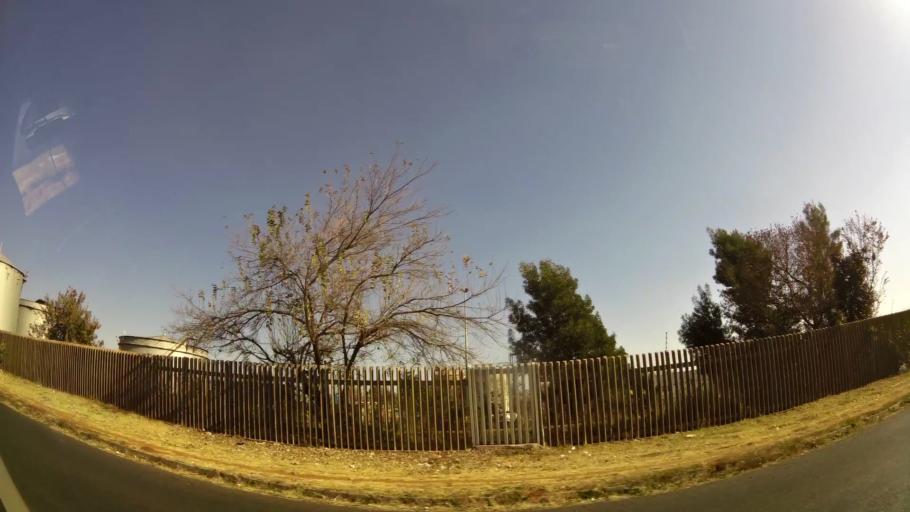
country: ZA
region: Gauteng
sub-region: City of Johannesburg Metropolitan Municipality
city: Johannesburg
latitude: -26.1976
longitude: 27.9776
